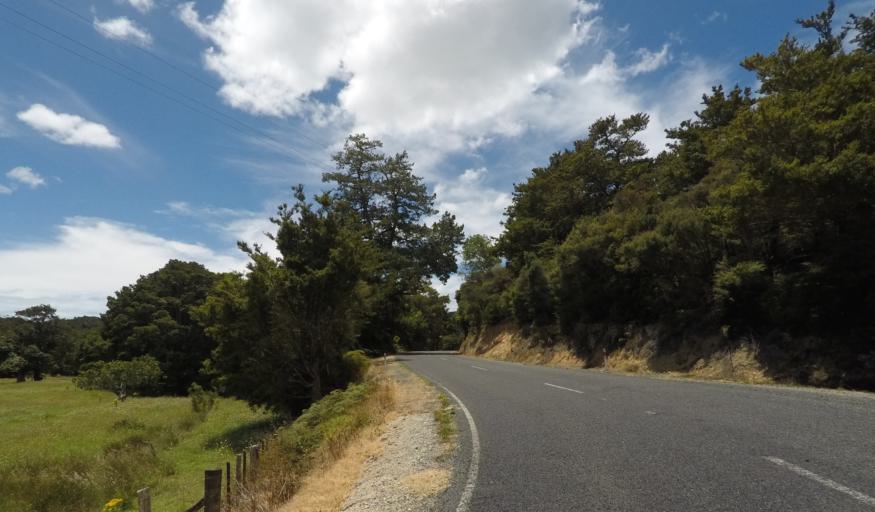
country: NZ
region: Northland
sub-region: Whangarei
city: Ngunguru
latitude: -35.5067
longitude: 174.4237
